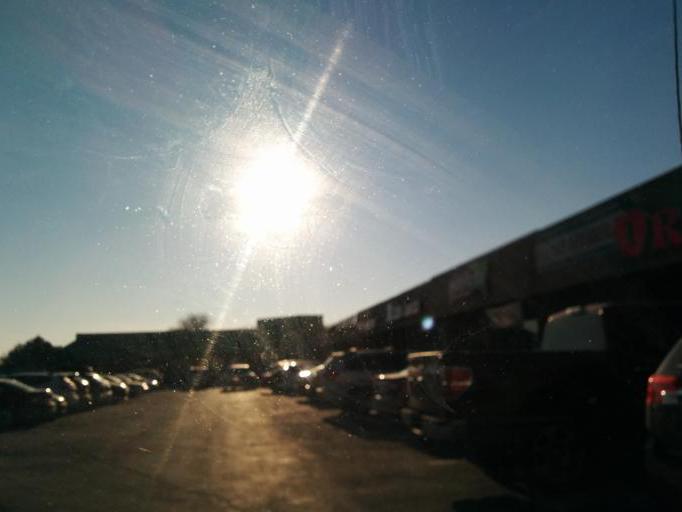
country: CA
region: Ontario
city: Mississauga
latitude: 43.5788
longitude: -79.6151
